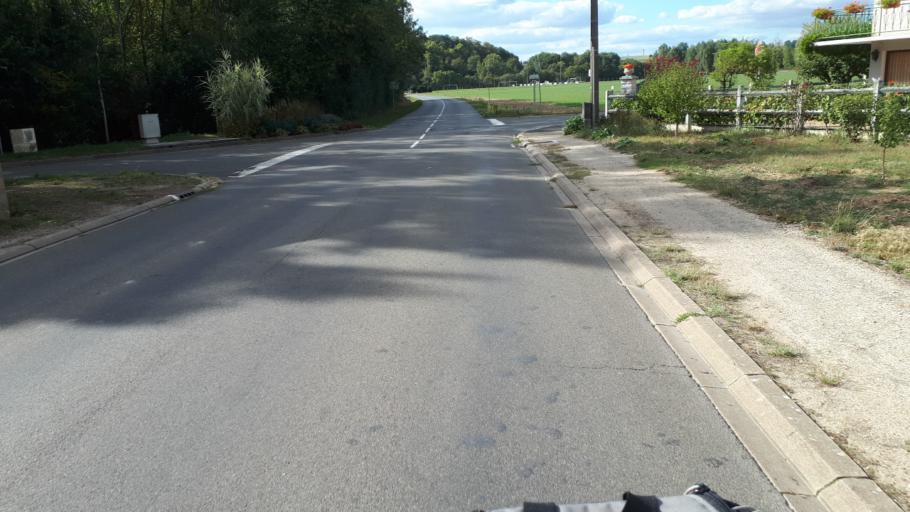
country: FR
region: Centre
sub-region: Departement du Loir-et-Cher
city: Villiers-sur-Loir
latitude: 47.7927
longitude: 0.9599
